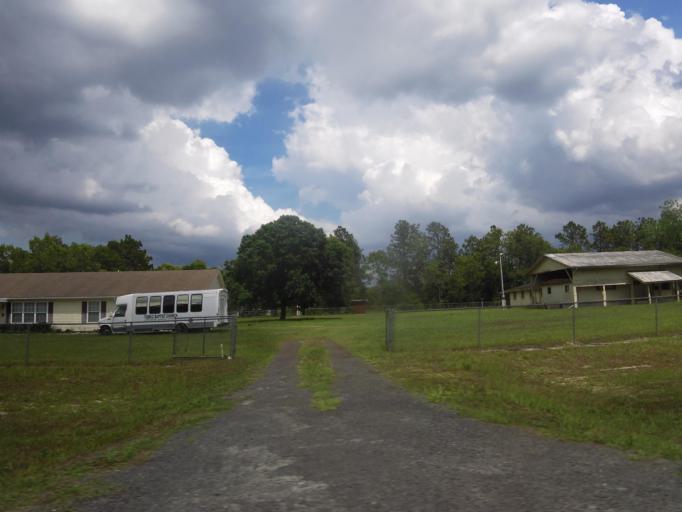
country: US
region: Florida
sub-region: Duval County
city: Baldwin
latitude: 30.3243
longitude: -81.8694
